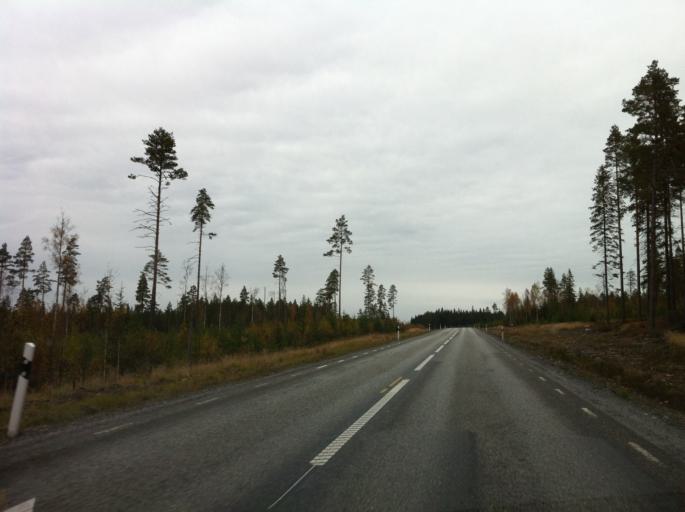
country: SE
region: OErebro
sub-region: Ljusnarsbergs Kommun
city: Kopparberg
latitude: 59.9562
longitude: 15.0207
